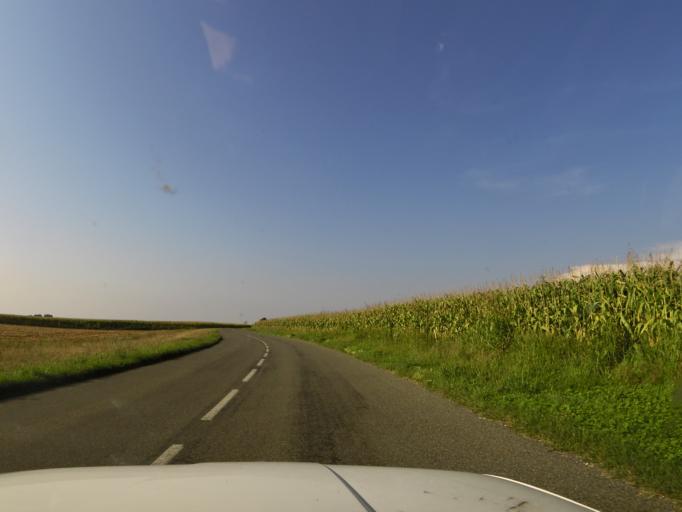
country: FR
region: Rhone-Alpes
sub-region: Departement de l'Ain
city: Chazey-sur-Ain
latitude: 45.8599
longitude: 5.2486
